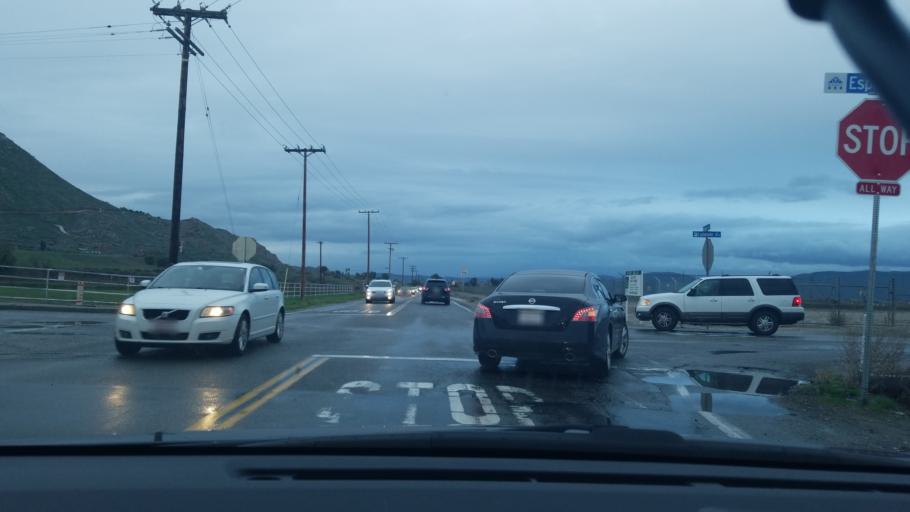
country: US
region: California
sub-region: Riverside County
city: Green Acres
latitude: 33.7728
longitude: -117.0334
